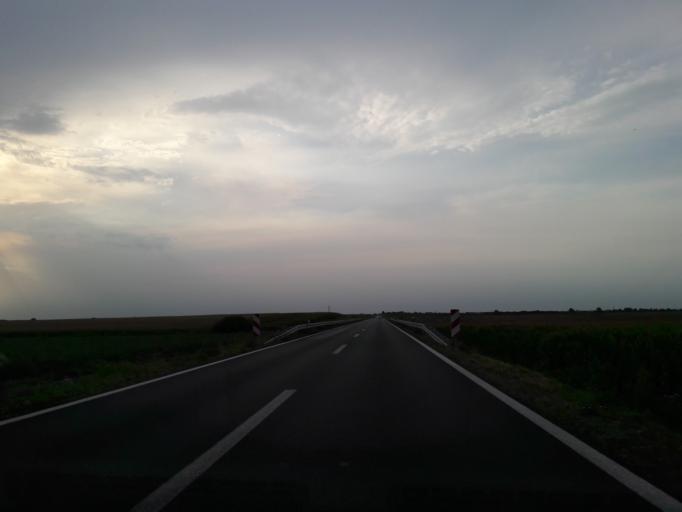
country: HR
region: Osjecko-Baranjska
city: Sarvas
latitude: 45.5040
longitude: 18.7994
